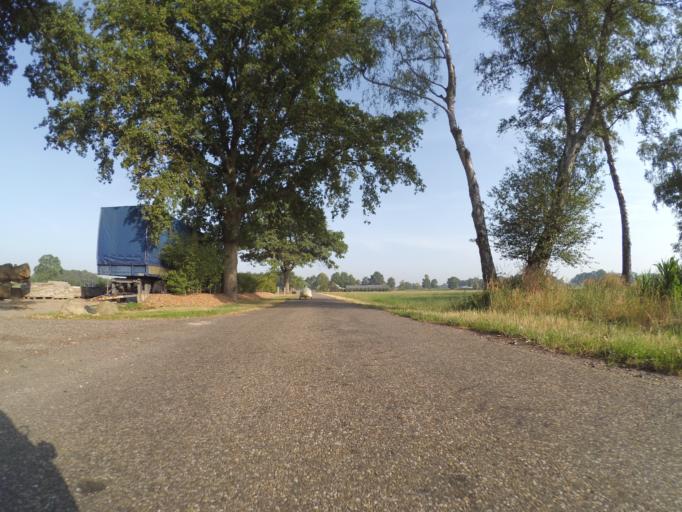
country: NL
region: Overijssel
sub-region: Gemeente Wierden
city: Wierden
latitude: 52.3206
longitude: 6.6172
